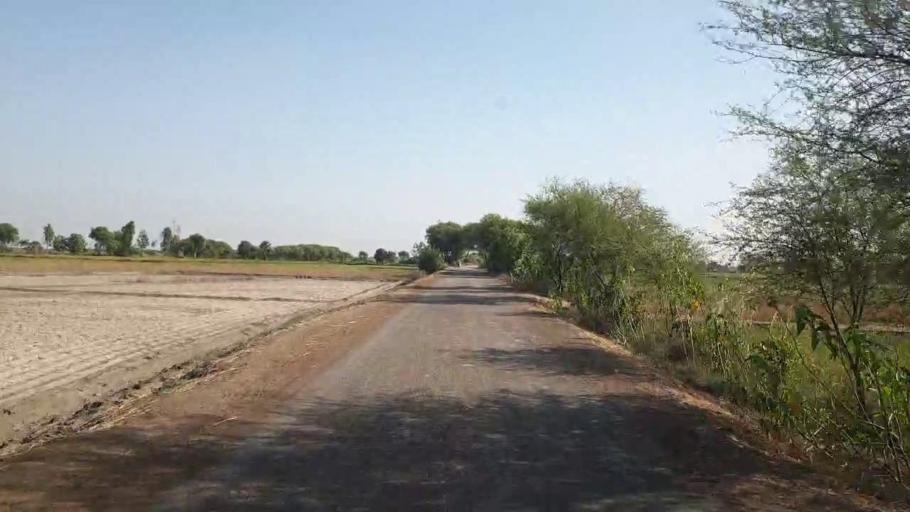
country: PK
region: Sindh
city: Matli
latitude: 25.0355
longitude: 68.7297
